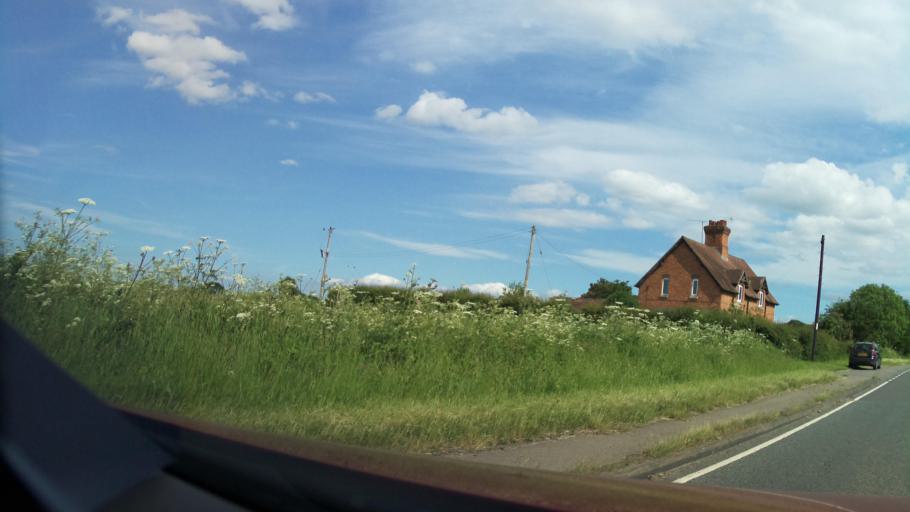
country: GB
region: England
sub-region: Worcestershire
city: Pershore
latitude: 52.1207
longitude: -2.1017
